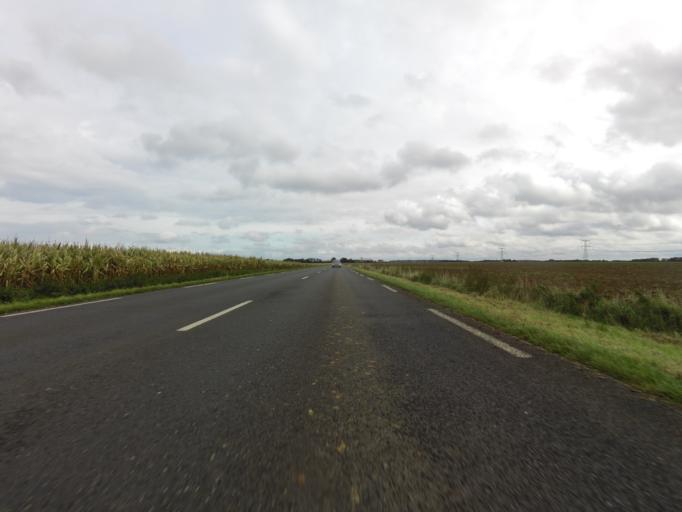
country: FR
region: Haute-Normandie
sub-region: Departement de la Seine-Maritime
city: Le Treport
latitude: 50.0212
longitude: 1.3709
